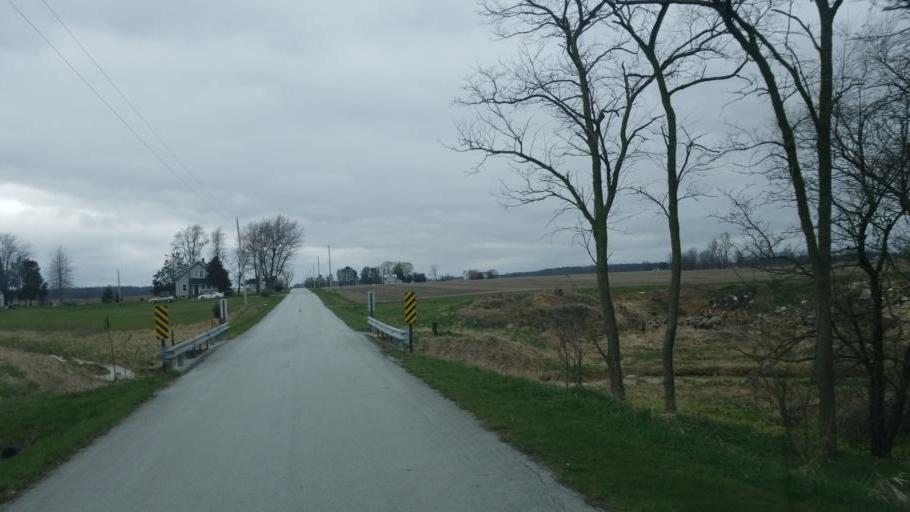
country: US
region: Ohio
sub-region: Hardin County
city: Forest
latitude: 40.7235
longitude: -83.5002
